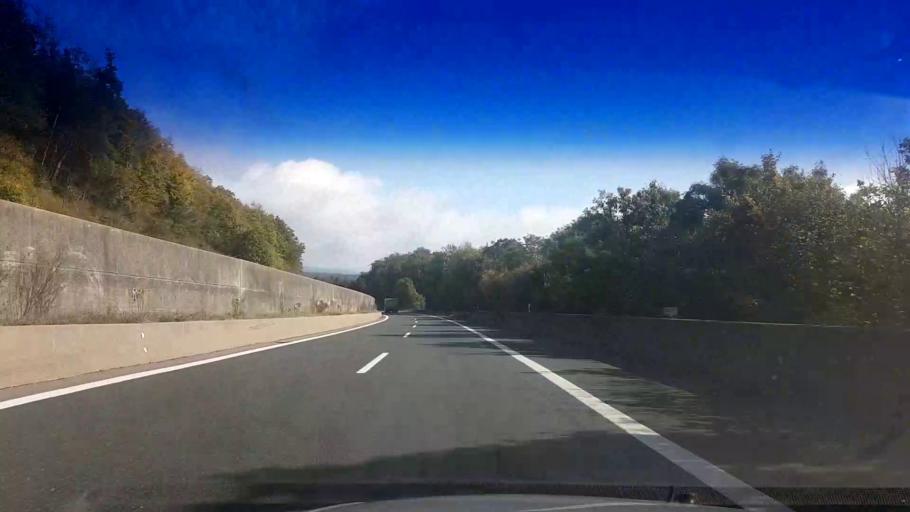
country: DE
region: Bavaria
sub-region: Upper Franconia
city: Thurnau
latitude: 50.0122
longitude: 11.3694
